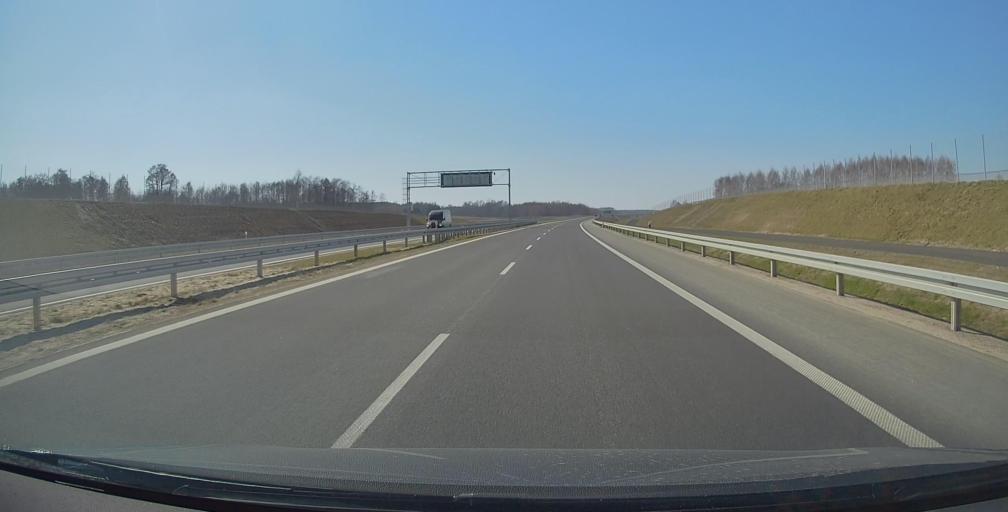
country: PL
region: Subcarpathian Voivodeship
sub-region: Powiat rzeszowski
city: Kamien
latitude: 50.3199
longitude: 22.1778
